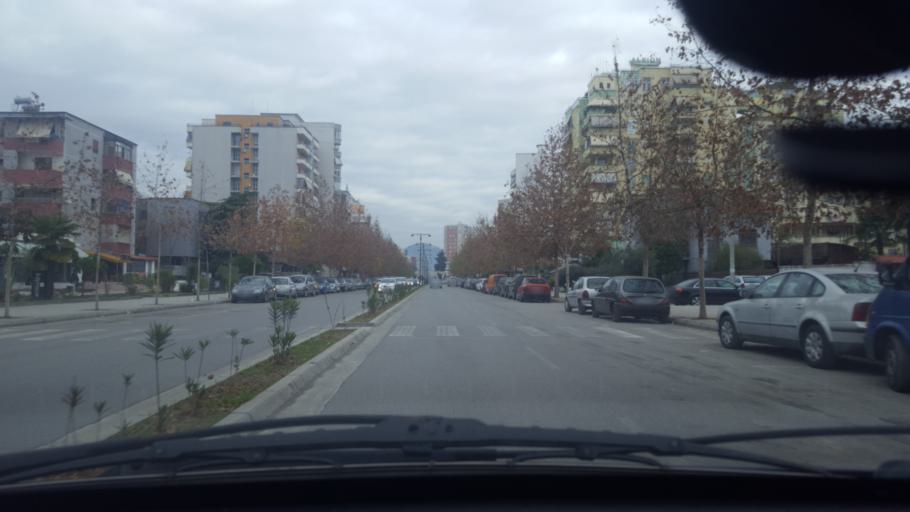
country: AL
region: Elbasan
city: Elbasan
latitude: 41.1099
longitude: 20.0759
